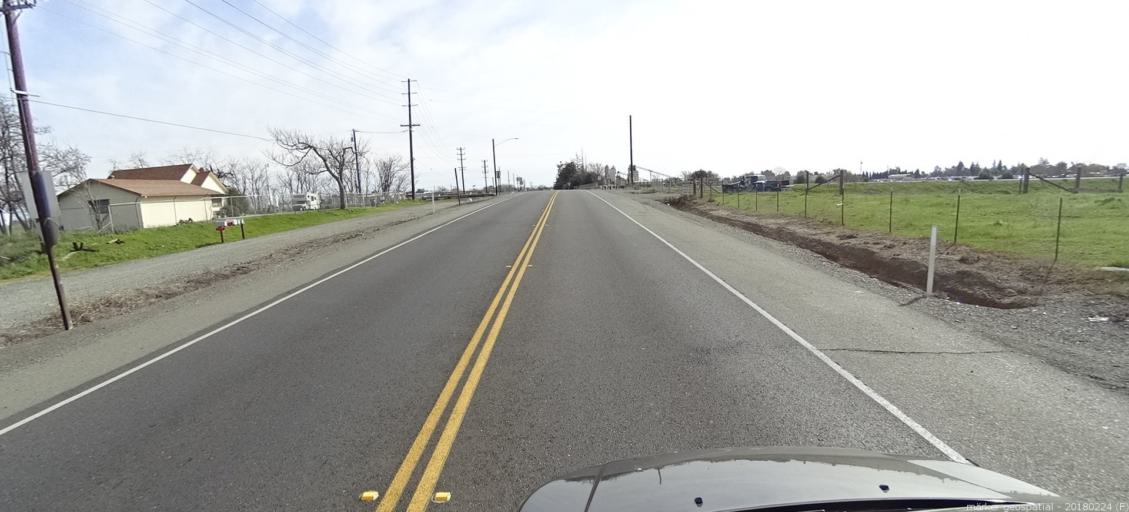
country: US
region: California
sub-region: Sacramento County
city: Elverta
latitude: 38.6851
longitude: -121.4866
